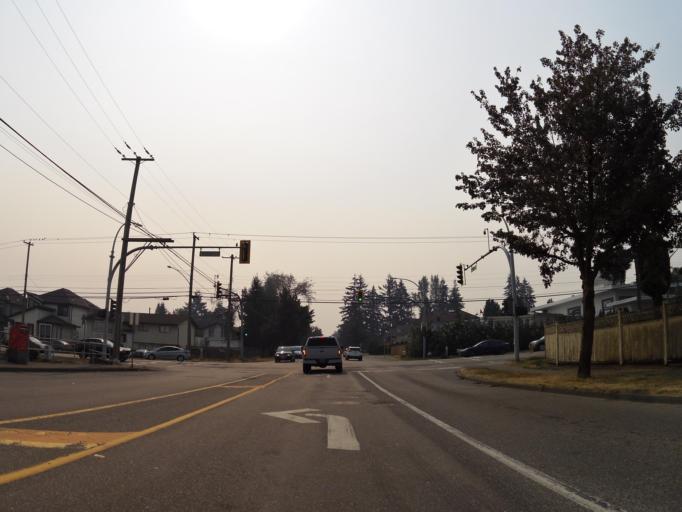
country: CA
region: British Columbia
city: Delta
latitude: 49.1487
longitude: -122.8790
